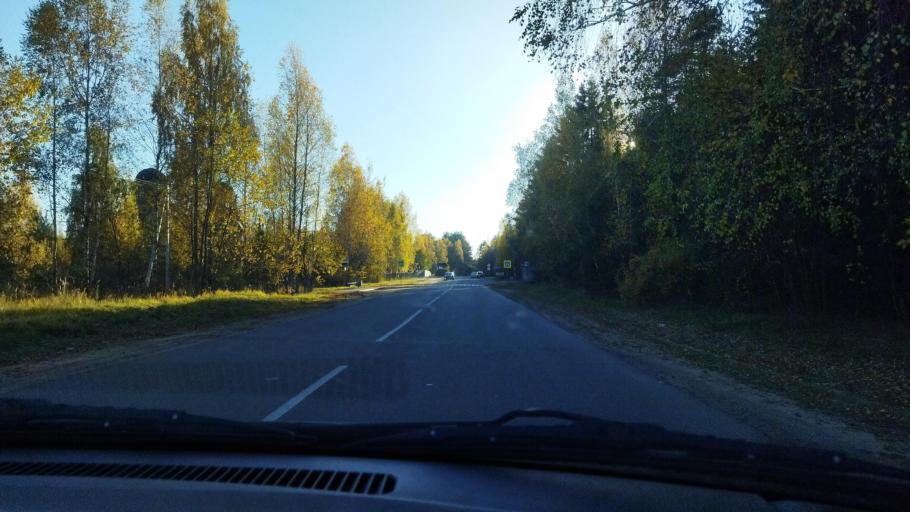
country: BY
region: Minsk
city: Kalodzishchy
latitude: 53.9205
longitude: 27.7546
